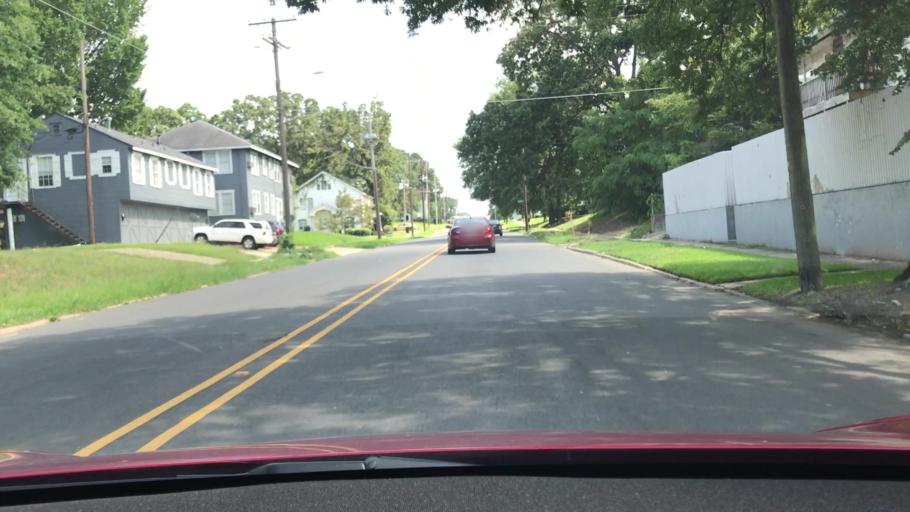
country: US
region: Louisiana
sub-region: Bossier Parish
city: Bossier City
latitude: 32.4915
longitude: -93.7332
